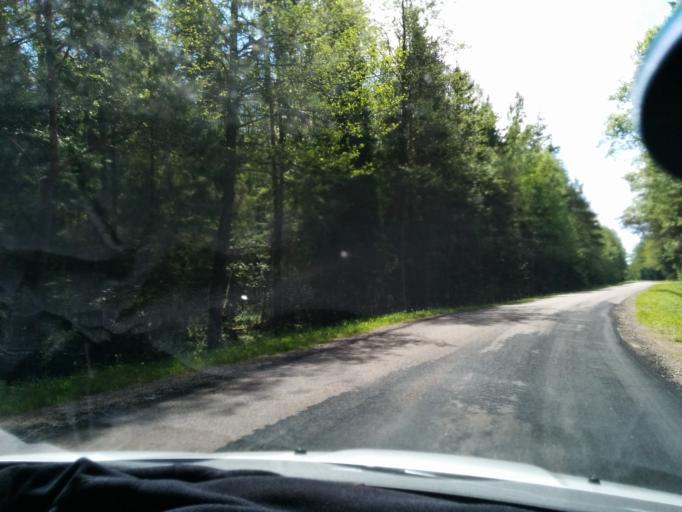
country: EE
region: Harju
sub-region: Loksa linn
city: Loksa
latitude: 59.5900
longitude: 25.9090
